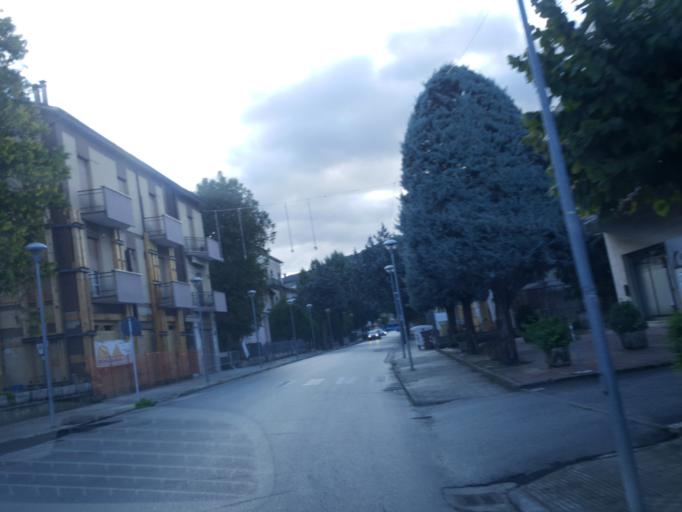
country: IT
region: The Marches
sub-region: Provincia di Macerata
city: Castelraimondo
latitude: 43.2086
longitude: 13.0533
